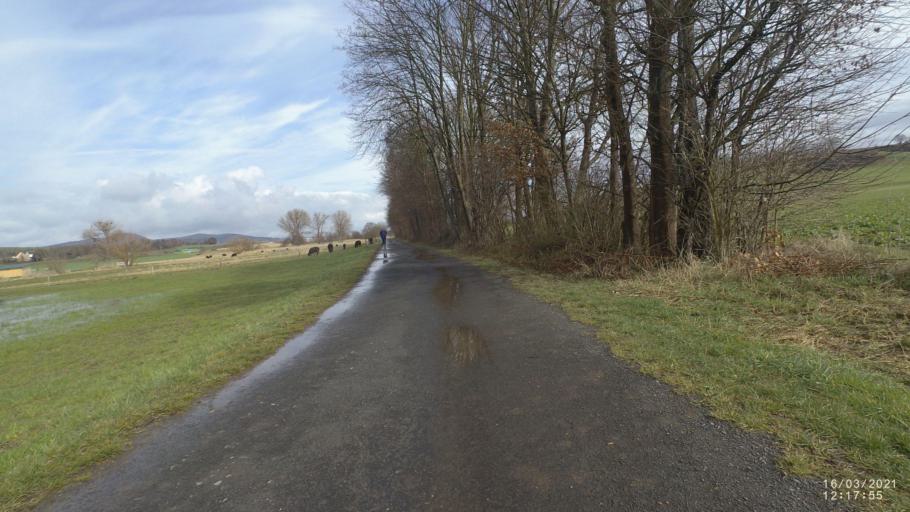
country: DE
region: Rheinland-Pfalz
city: Thur
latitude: 50.3513
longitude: 7.2856
